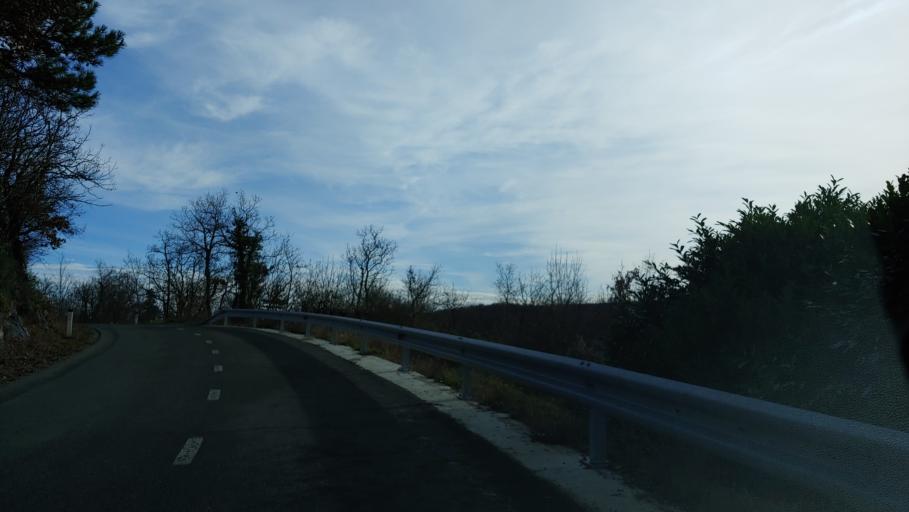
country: IT
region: Friuli Venezia Giulia
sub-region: Provincia di Trieste
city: Sistiana-Visogliano
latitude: 45.8102
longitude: 13.6526
